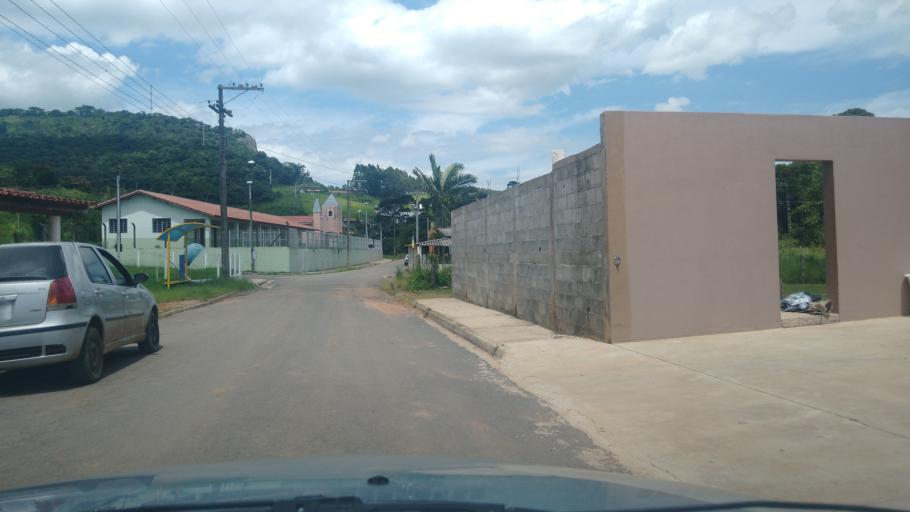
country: BR
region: Minas Gerais
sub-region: Extrema
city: Extrema
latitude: -22.7288
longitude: -46.3150
